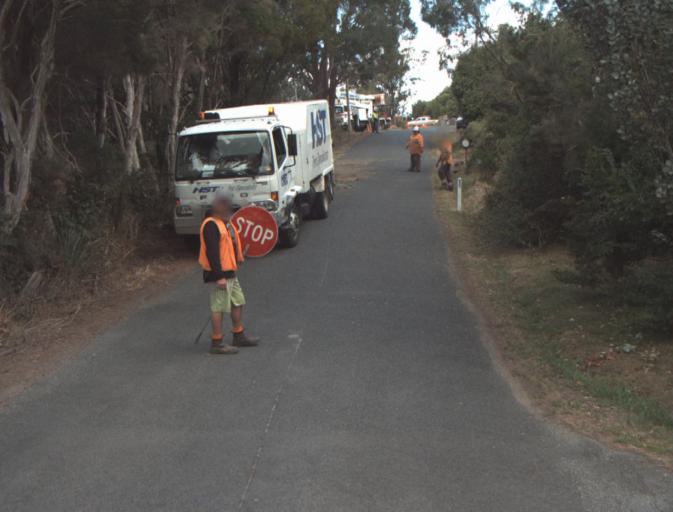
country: AU
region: Tasmania
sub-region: Launceston
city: Mayfield
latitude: -41.3015
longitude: 147.0347
